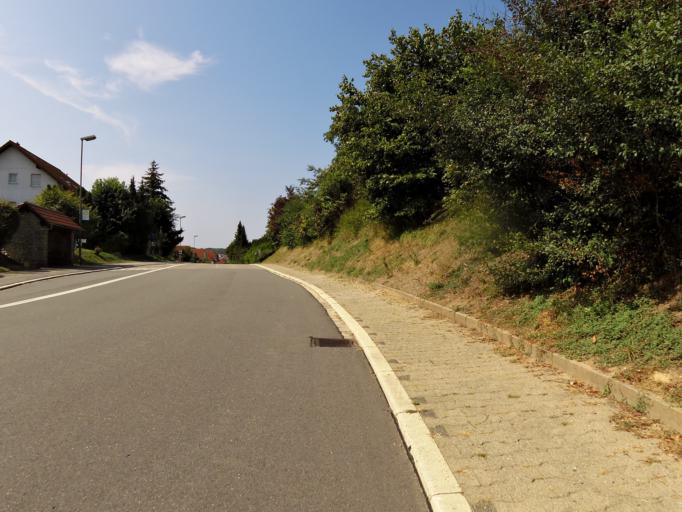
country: DE
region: Baden-Wuerttemberg
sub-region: Karlsruhe Region
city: Neidenstein
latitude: 49.3170
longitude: 8.8831
